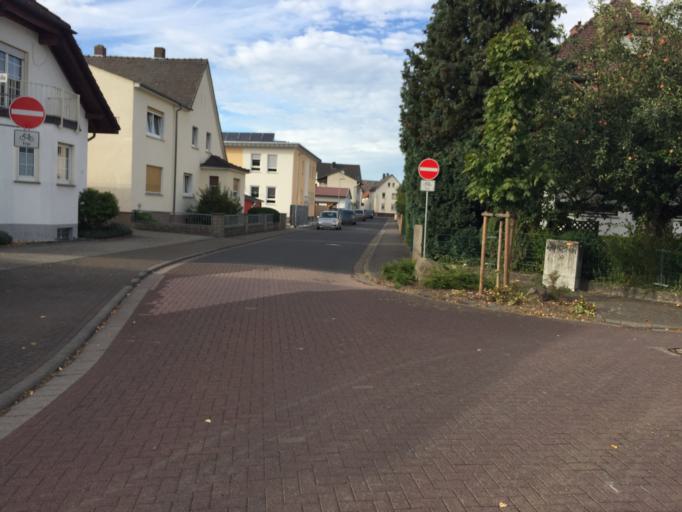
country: DE
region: Hesse
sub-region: Regierungsbezirk Giessen
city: Langgons
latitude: 50.5324
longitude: 8.7118
